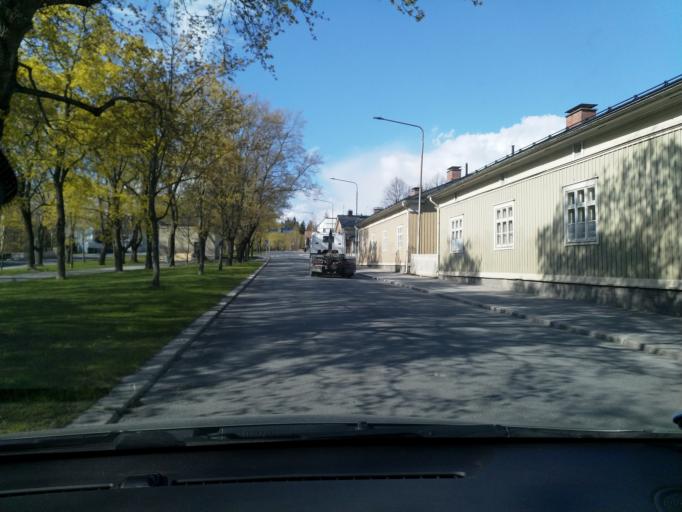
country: FI
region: Pirkanmaa
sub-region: Tampere
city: Tampere
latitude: 61.5033
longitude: 23.7870
